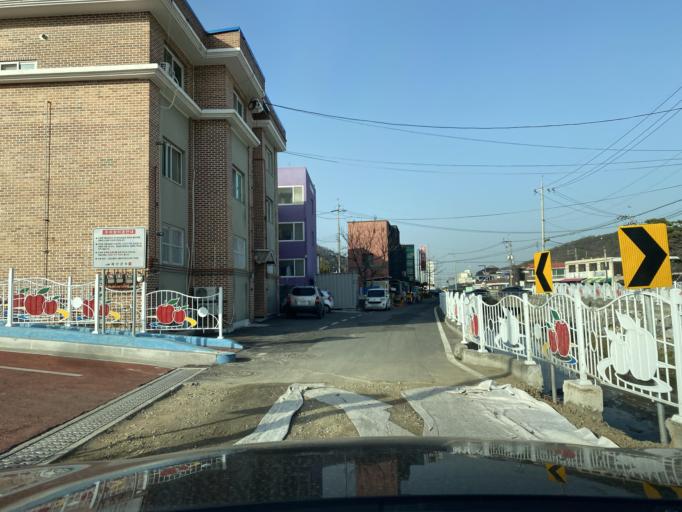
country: KR
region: Chungcheongnam-do
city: Yesan
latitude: 36.6759
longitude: 126.8479
